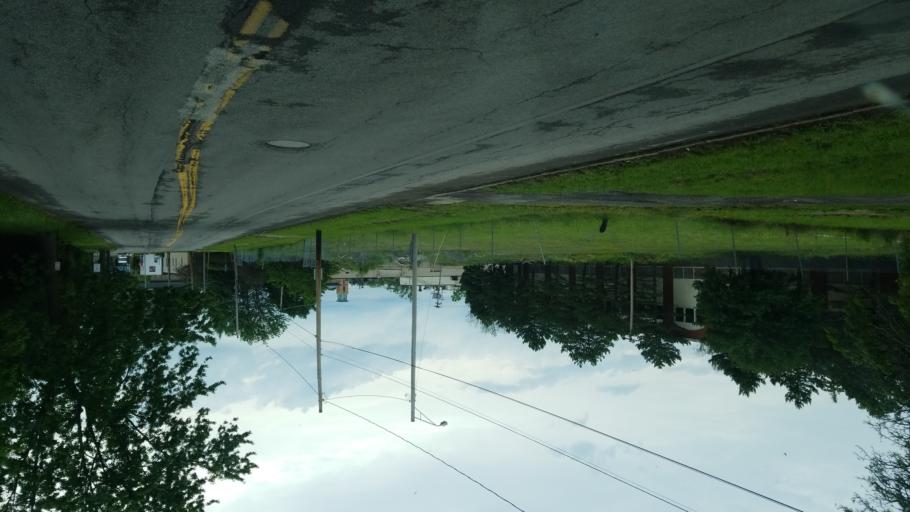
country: CA
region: Ontario
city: Niagara Falls
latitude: 43.1126
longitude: -79.0568
